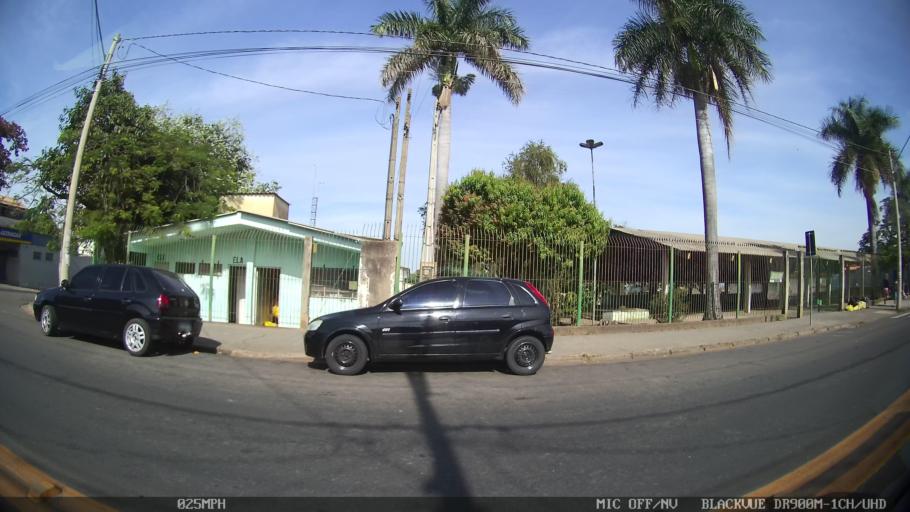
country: BR
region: Sao Paulo
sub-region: Piracicaba
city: Piracicaba
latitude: -22.7493
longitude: -47.6553
